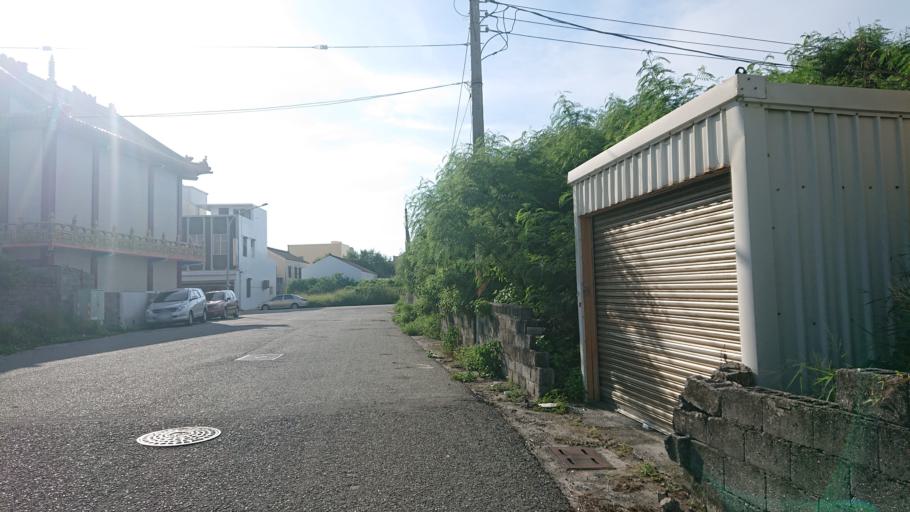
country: TW
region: Taiwan
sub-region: Penghu
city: Ma-kung
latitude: 23.5239
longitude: 119.6020
